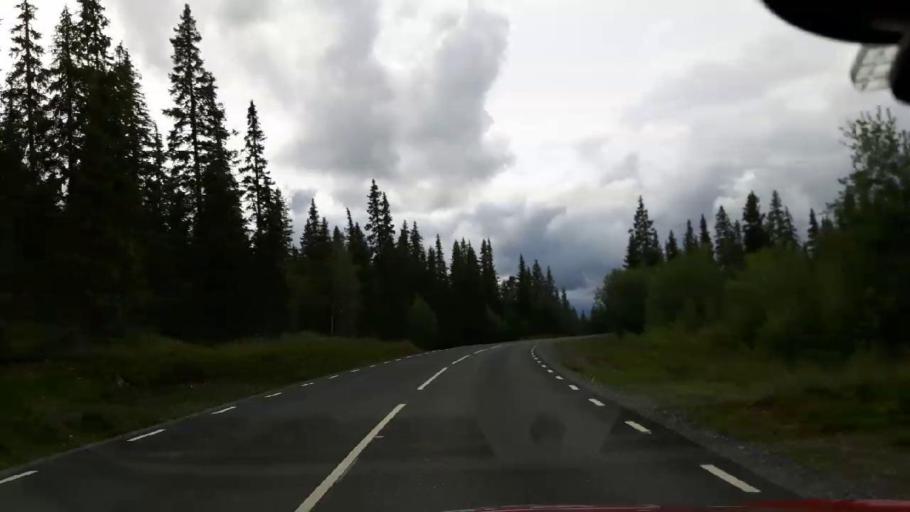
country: NO
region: Nord-Trondelag
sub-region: Lierne
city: Sandvika
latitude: 64.5964
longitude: 14.1186
